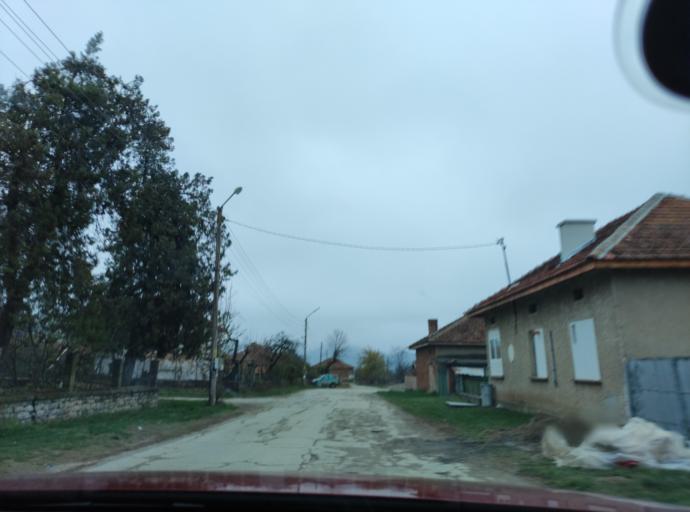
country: BG
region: Lovech
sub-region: Obshtina Yablanitsa
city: Yablanitsa
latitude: 43.0924
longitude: 24.0797
